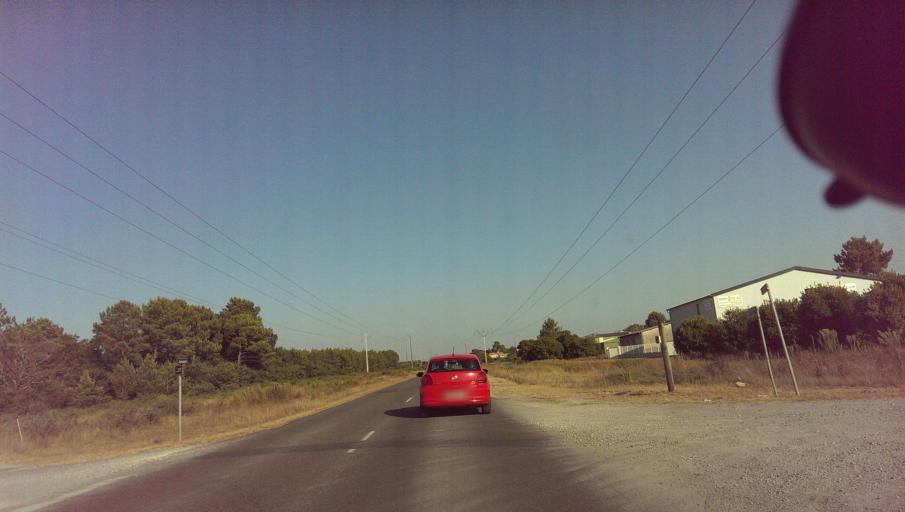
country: FR
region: Aquitaine
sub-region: Departement des Landes
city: Mimizan
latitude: 44.1908
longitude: -1.2156
